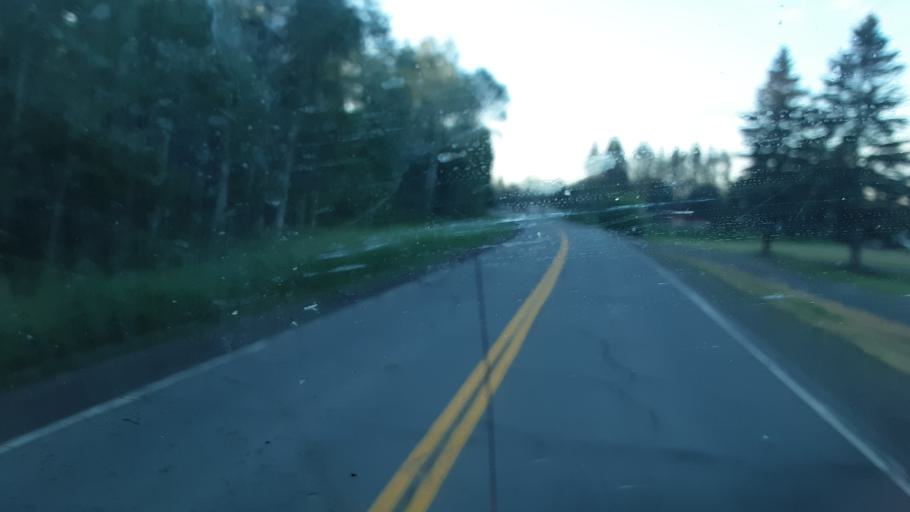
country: US
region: Maine
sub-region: Aroostook County
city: Presque Isle
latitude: 46.7473
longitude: -68.0472
